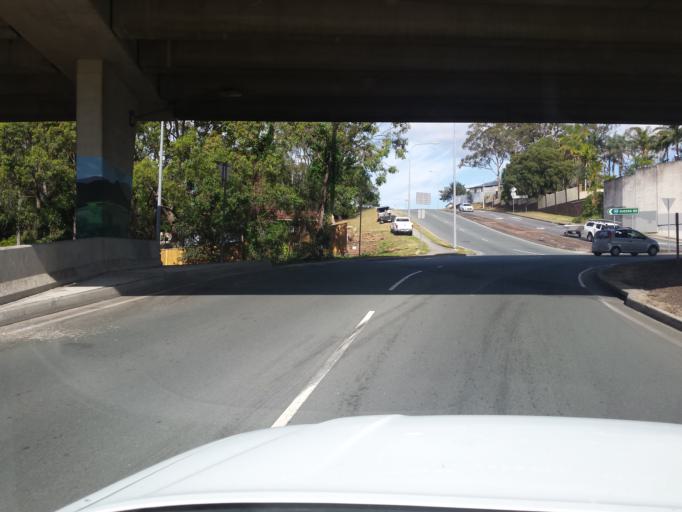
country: AU
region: Queensland
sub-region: Brisbane
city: Everton Park
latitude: -27.3861
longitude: 152.9849
